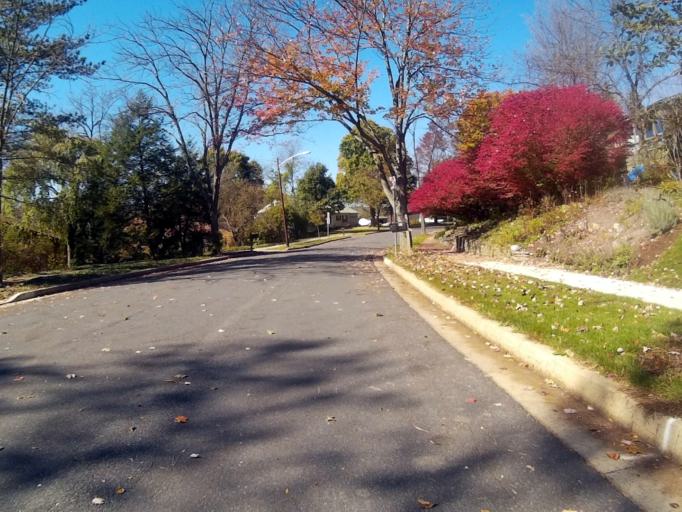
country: US
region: Pennsylvania
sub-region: Centre County
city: State College
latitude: 40.7937
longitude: -77.8814
